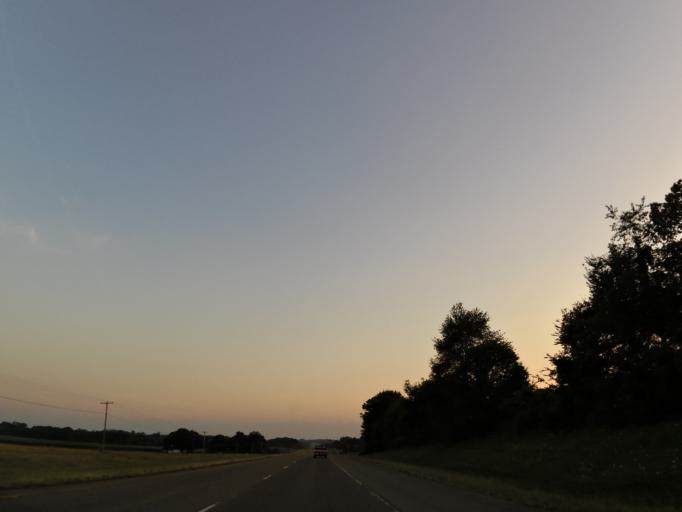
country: US
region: Tennessee
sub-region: Carroll County
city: McKenzie
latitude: 36.1697
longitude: -88.4502
